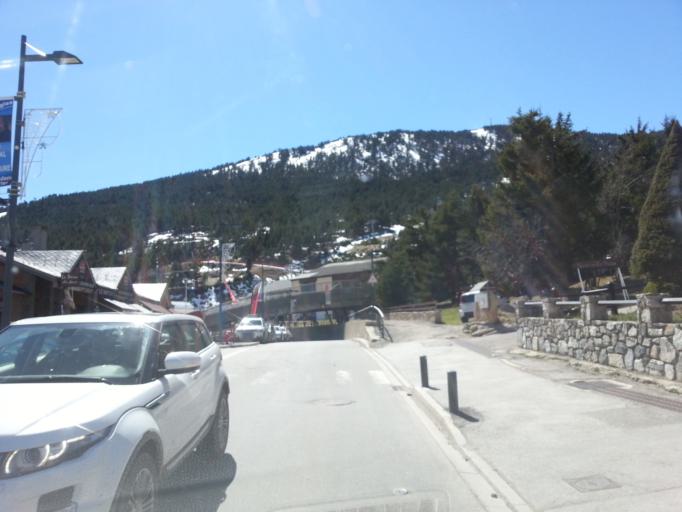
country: ES
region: Catalonia
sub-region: Provincia de Girona
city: Llivia
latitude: 42.5764
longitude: 2.0702
